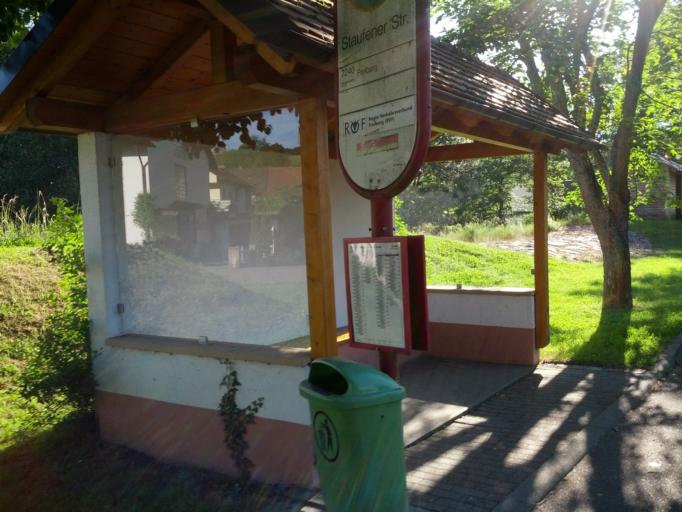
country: DE
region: Baden-Wuerttemberg
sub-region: Freiburg Region
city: Pfaffenweiler
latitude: 47.9373
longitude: 7.7506
